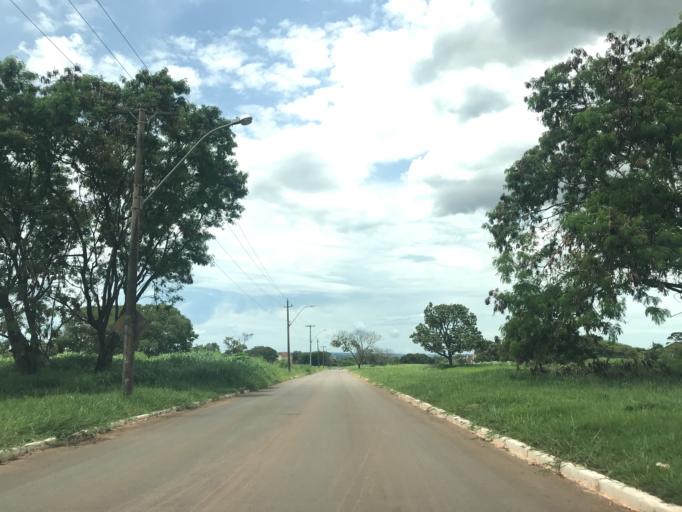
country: BR
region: Federal District
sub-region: Brasilia
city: Brasilia
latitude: -15.8318
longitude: -47.9038
